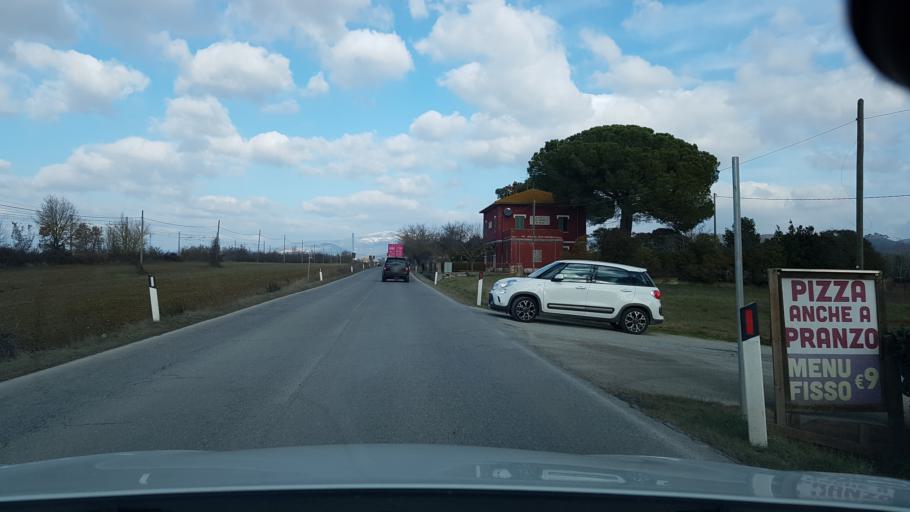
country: IT
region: Tuscany
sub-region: Province of Arezzo
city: Terontola
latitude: 43.1765
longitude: 12.0139
